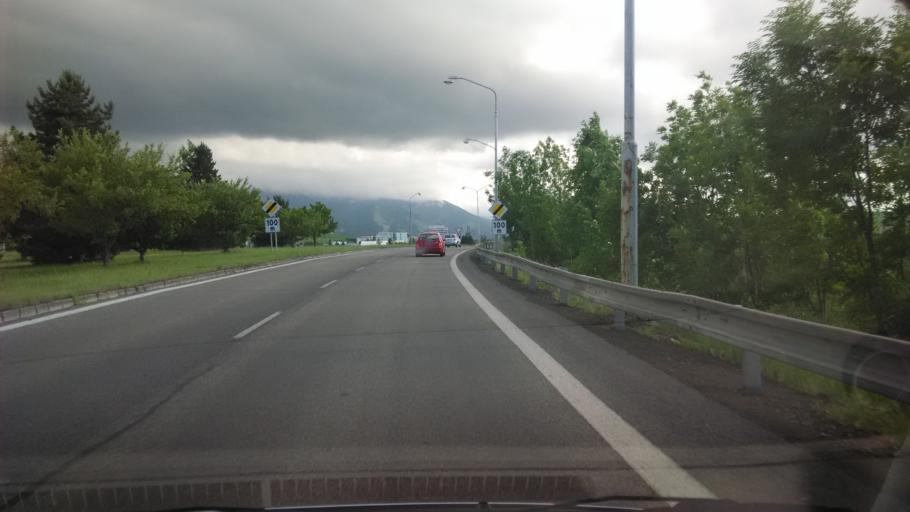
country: SK
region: Zilinsky
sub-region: Okres Liptovsky Mikulas
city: Liptovsky Mikulas
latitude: 49.0774
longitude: 19.5997
